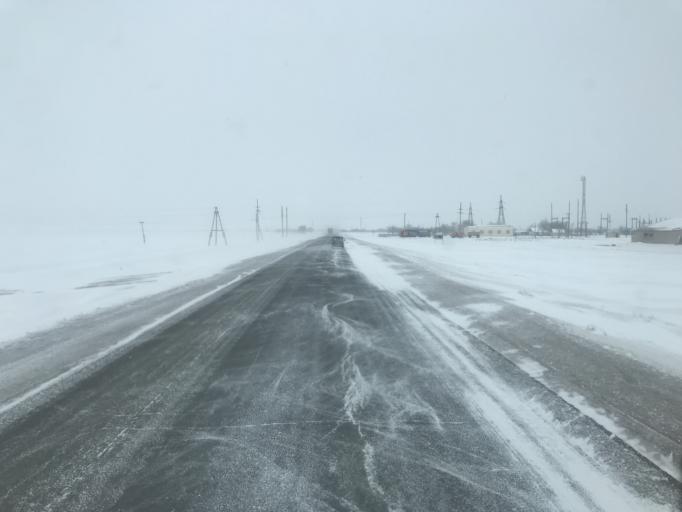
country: KZ
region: Batys Qazaqstan
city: Chapaev
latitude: 50.5147
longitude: 51.0586
